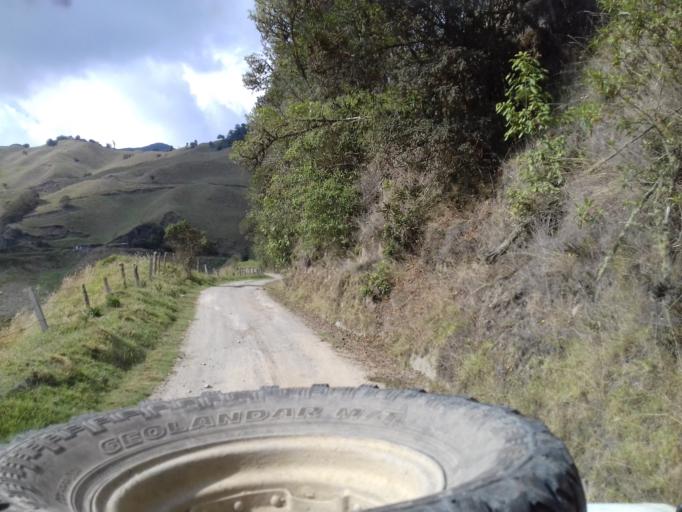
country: CO
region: Tolima
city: Cajamarca
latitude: 4.5447
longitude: -75.4901
